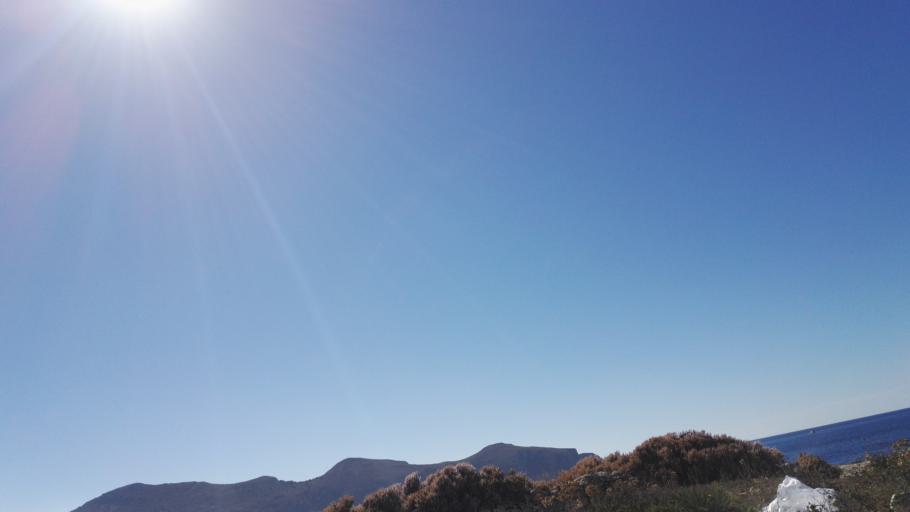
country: IT
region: Sicily
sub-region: Trapani
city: Favignana
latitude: 37.9358
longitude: 12.3444
